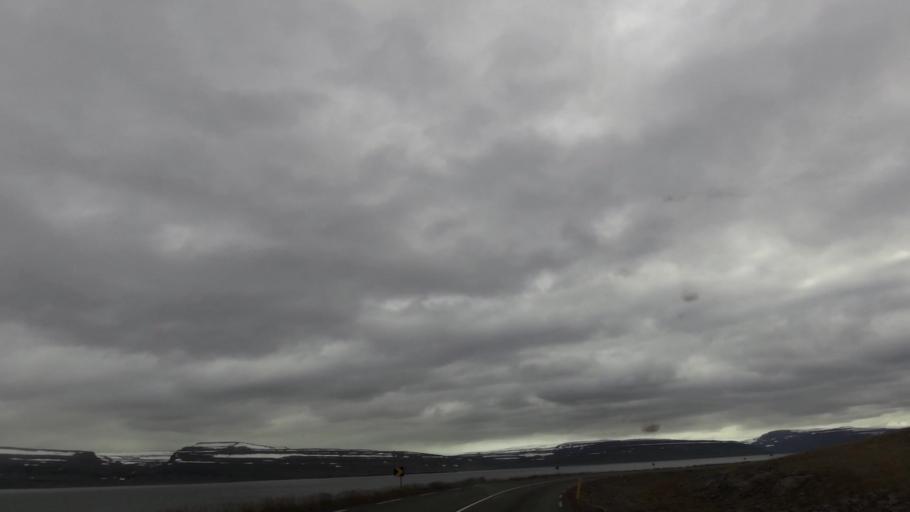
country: IS
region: Westfjords
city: Isafjoerdur
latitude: 66.0542
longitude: -22.7633
